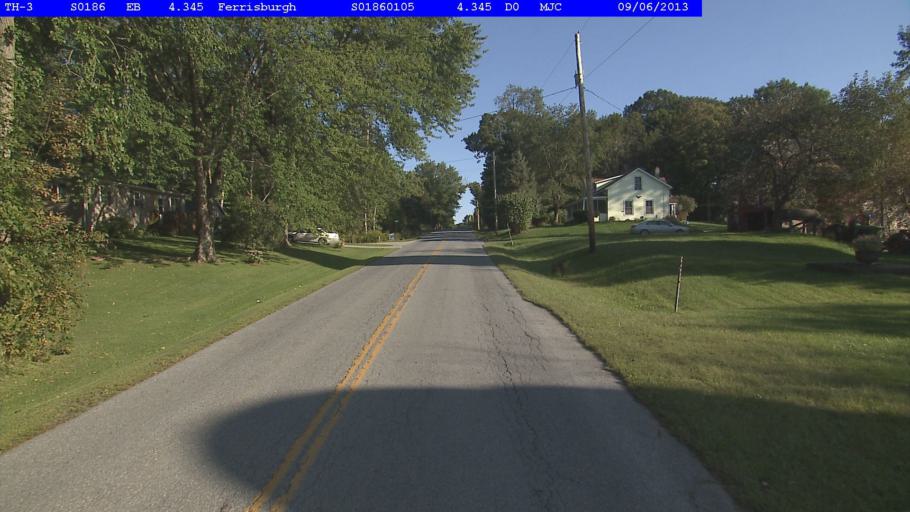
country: US
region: Vermont
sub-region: Addison County
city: Vergennes
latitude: 44.1666
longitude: -73.2973
